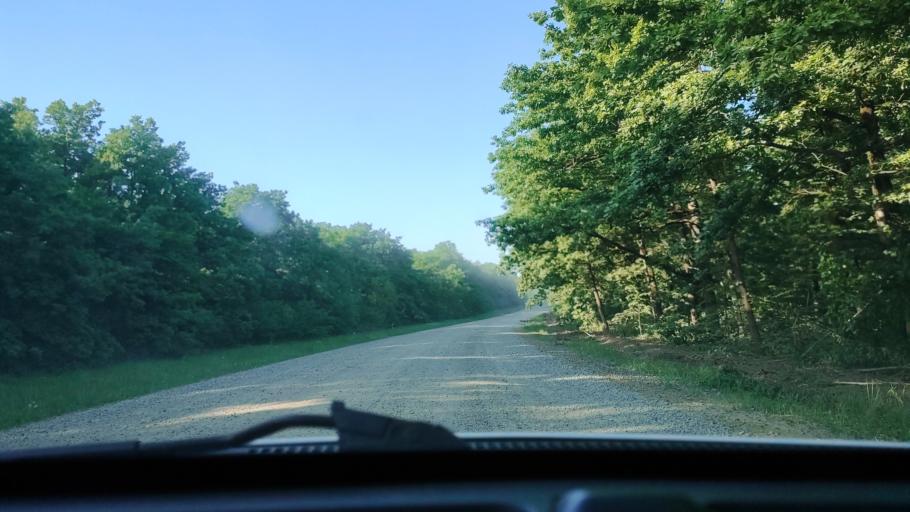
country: RU
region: Krasnodarskiy
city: Goryachiy Klyuch
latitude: 44.7040
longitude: 38.9887
